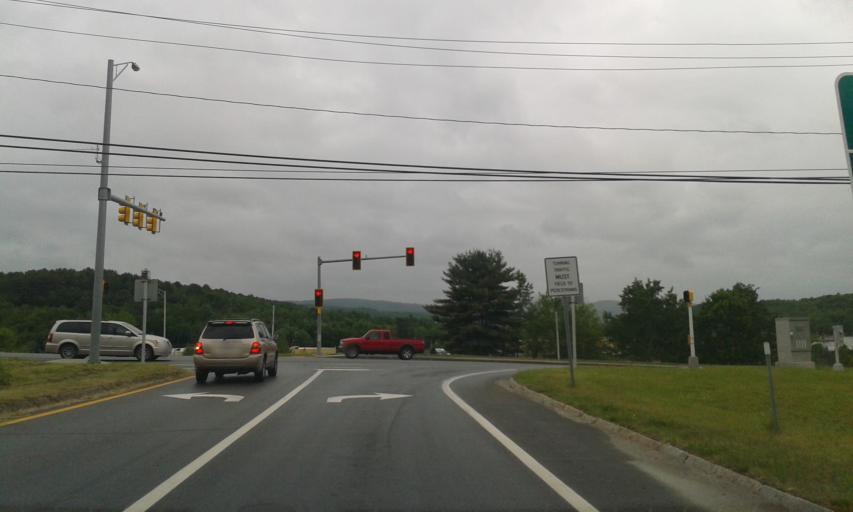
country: US
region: New Hampshire
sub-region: Grafton County
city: Littleton
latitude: 44.3085
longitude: -71.7999
